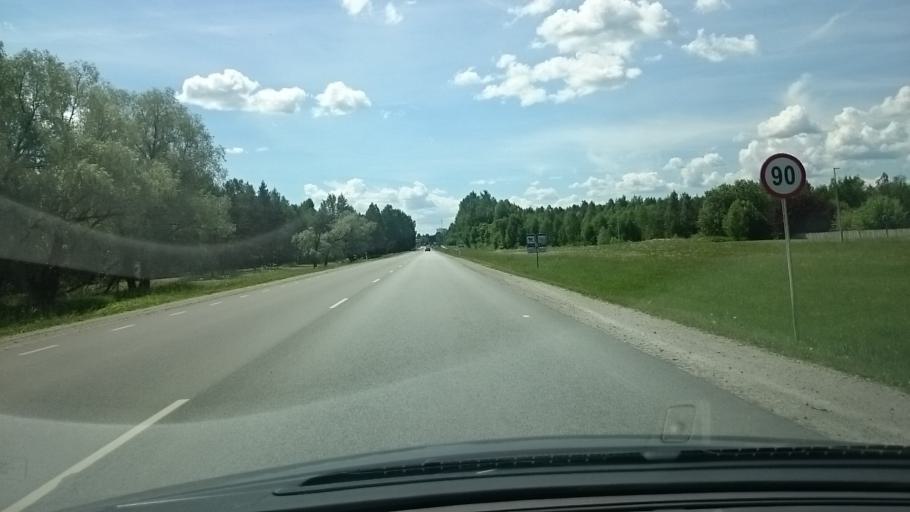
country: EE
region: Jaervamaa
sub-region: Paide linn
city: Paide
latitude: 58.9021
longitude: 25.5765
